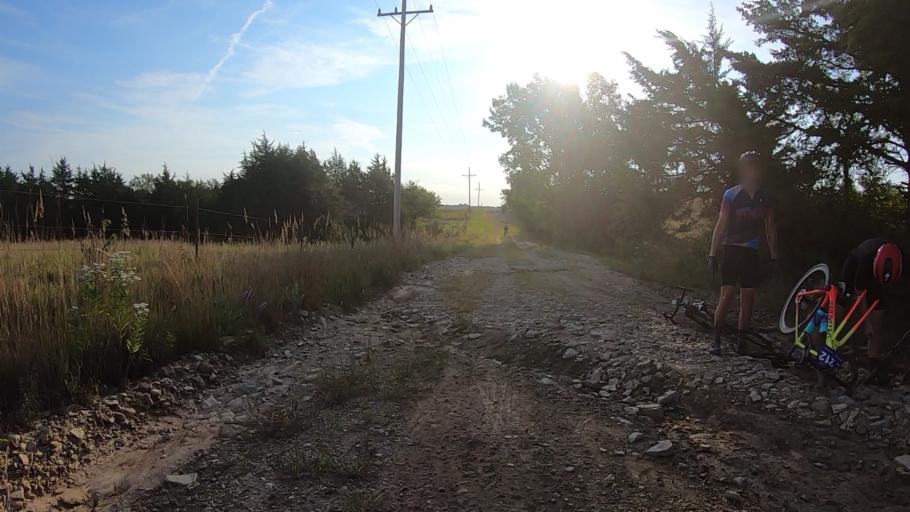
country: US
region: Kansas
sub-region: Marshall County
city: Blue Rapids
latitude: 39.7116
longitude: -96.7938
